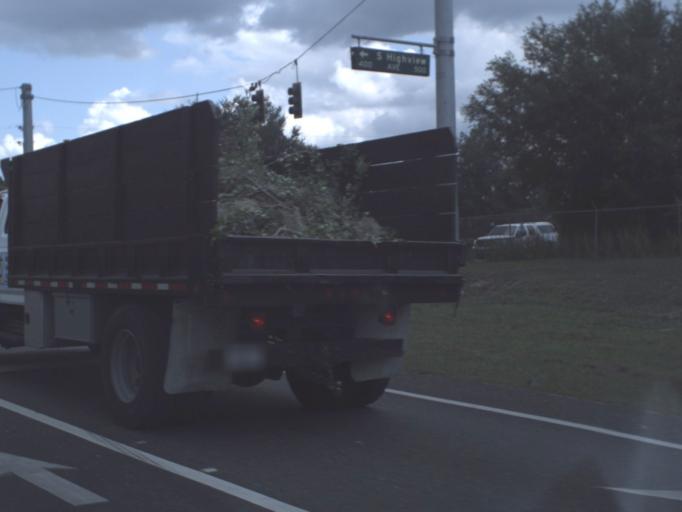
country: US
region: Florida
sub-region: Citrus County
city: Citrus Hills
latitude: 28.8558
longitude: -82.4397
